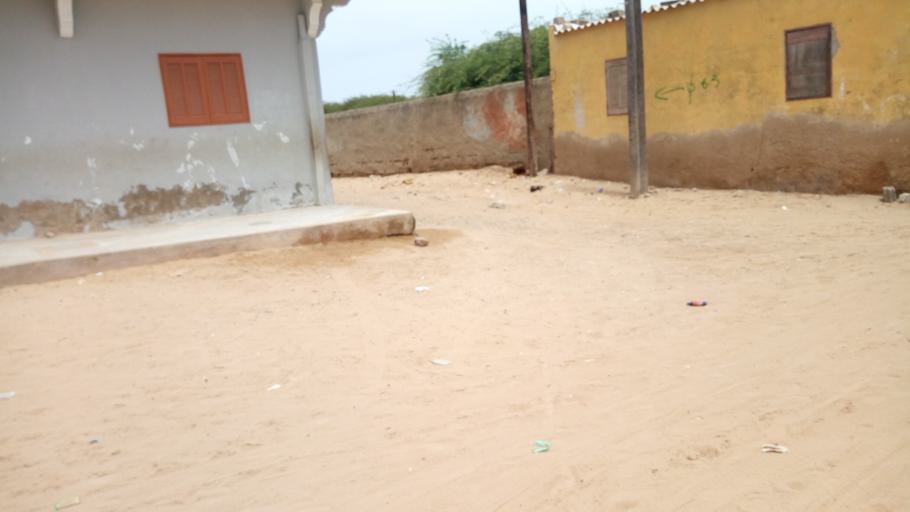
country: SN
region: Saint-Louis
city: Saint-Louis
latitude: 16.0128
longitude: -16.4857
